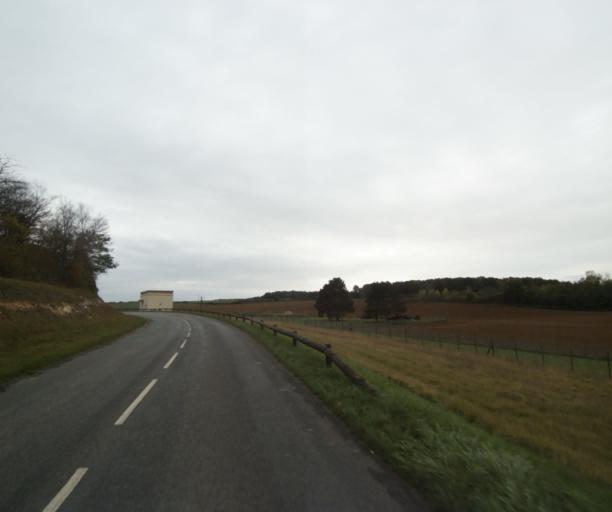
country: FR
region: Centre
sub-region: Departement d'Eure-et-Loir
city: Vert-en-Drouais
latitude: 48.7513
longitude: 1.3117
